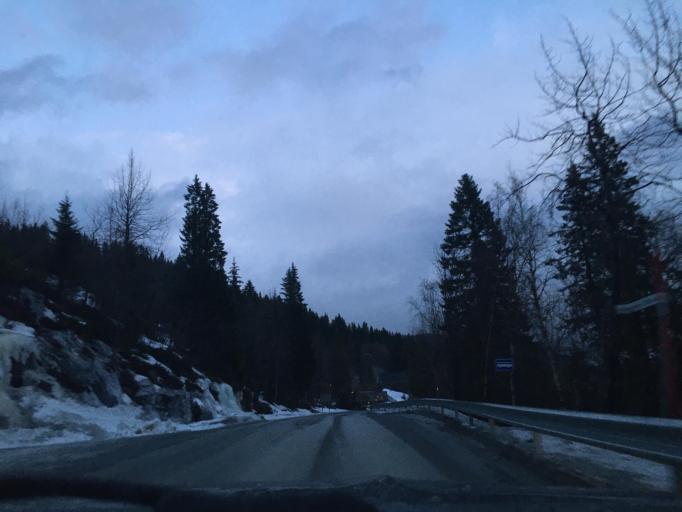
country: NO
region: Nordland
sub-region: Rana
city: Hauknes
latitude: 66.3051
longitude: 13.9569
